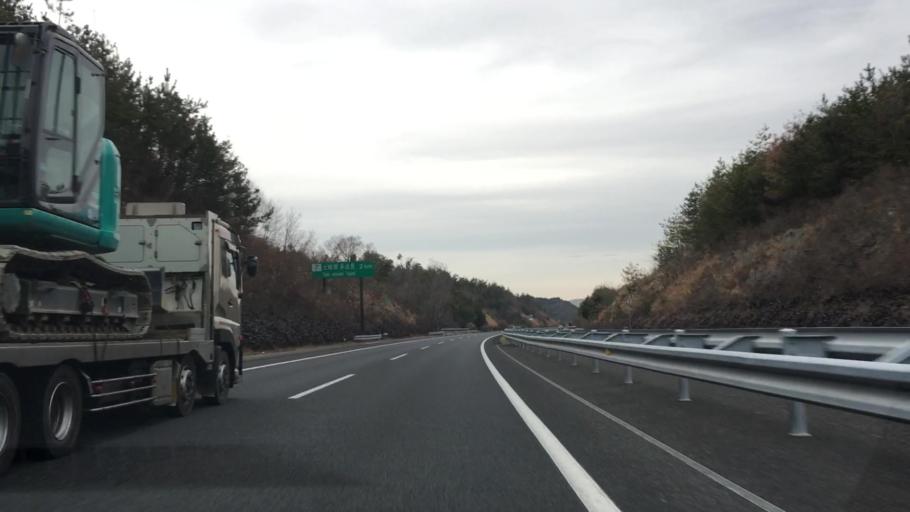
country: JP
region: Gifu
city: Toki
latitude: 35.3128
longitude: 137.1774
